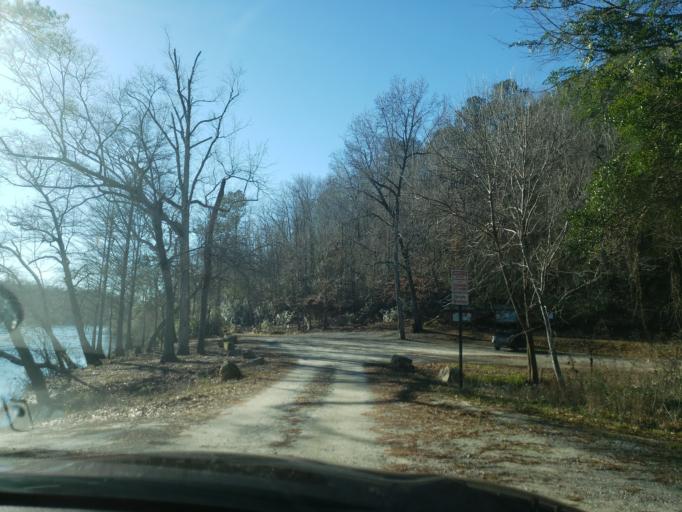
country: US
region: Alabama
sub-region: Elmore County
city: Eclectic
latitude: 32.6735
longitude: -85.9089
